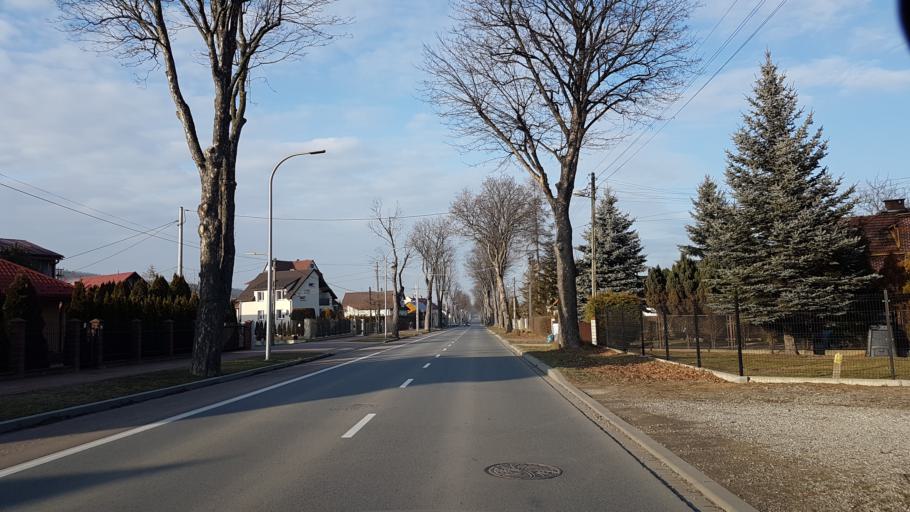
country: PL
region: Lesser Poland Voivodeship
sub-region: Powiat nowosadecki
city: Stary Sacz
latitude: 49.5478
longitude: 20.6420
